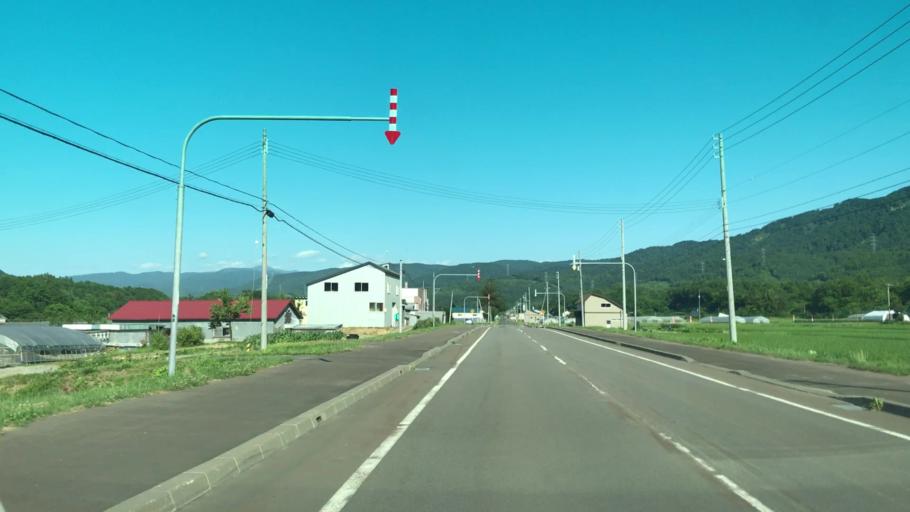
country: JP
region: Hokkaido
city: Yoichi
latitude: 43.0380
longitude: 140.7402
